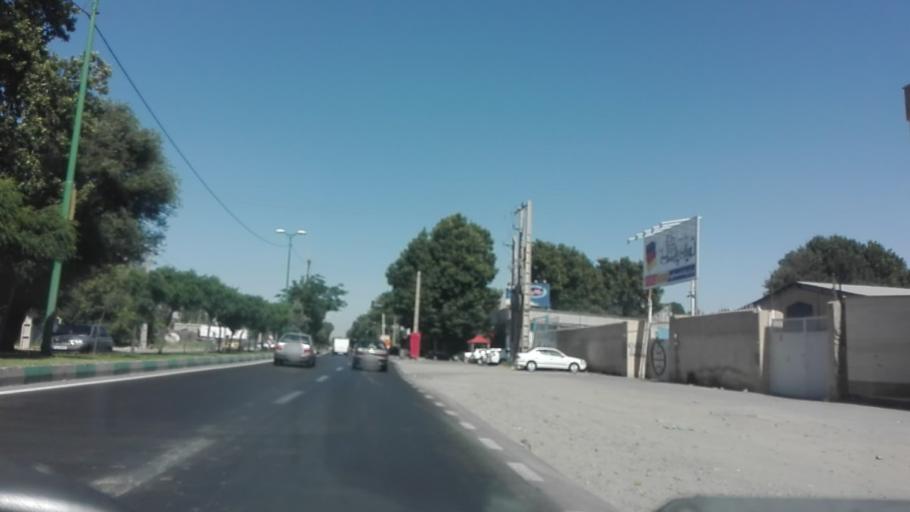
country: IR
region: Tehran
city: Shahriar
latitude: 35.6539
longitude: 51.0317
